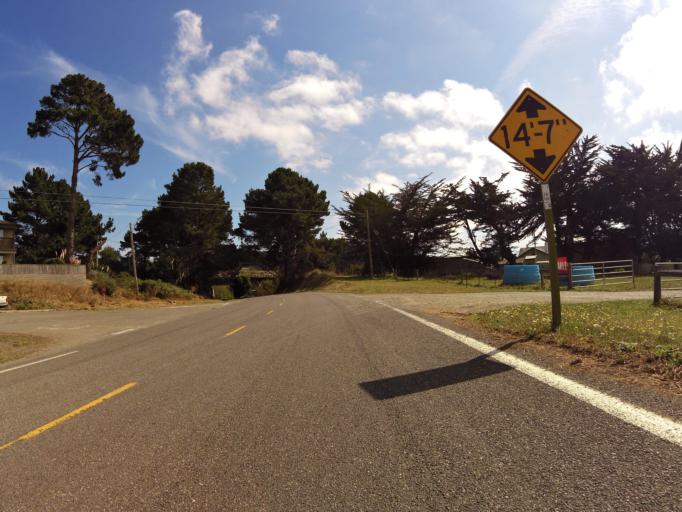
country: US
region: California
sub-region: Humboldt County
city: Ferndale
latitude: 40.6385
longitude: -124.2258
